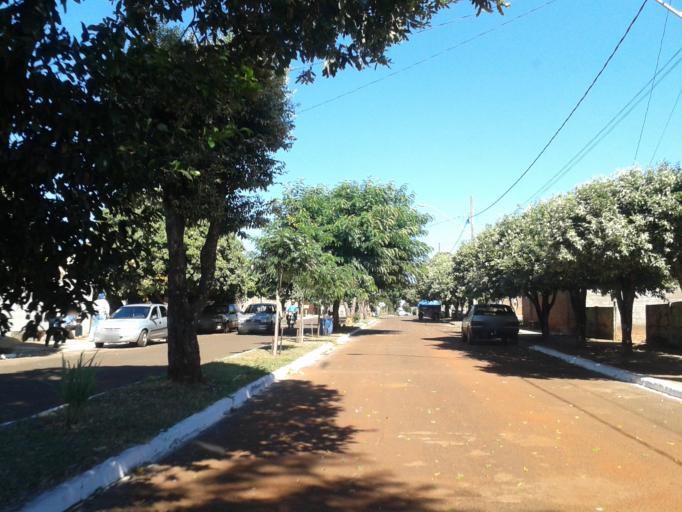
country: BR
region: Minas Gerais
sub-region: Santa Vitoria
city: Santa Vitoria
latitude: -18.8492
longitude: -50.1189
